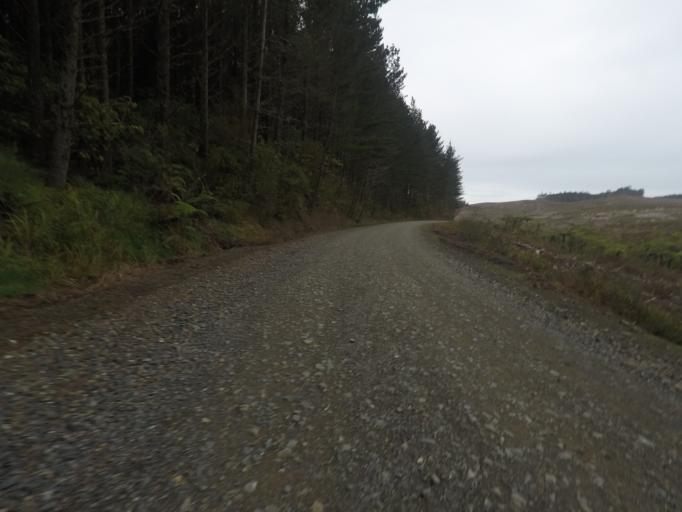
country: NZ
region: Auckland
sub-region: Auckland
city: Muriwai Beach
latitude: -36.7466
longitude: 174.5758
